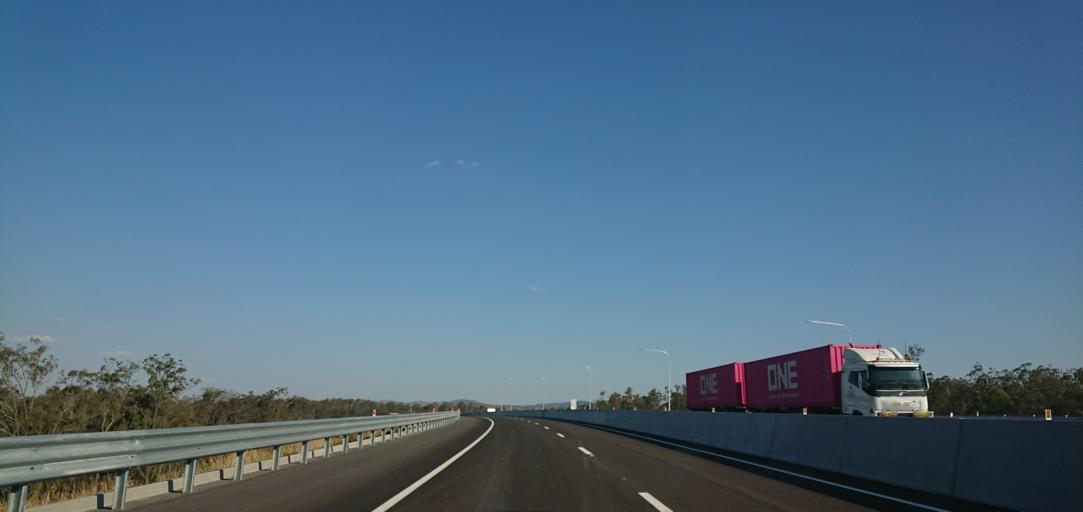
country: AU
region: Queensland
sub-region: Toowoomba
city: Rangeville
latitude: -27.5419
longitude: 152.0783
